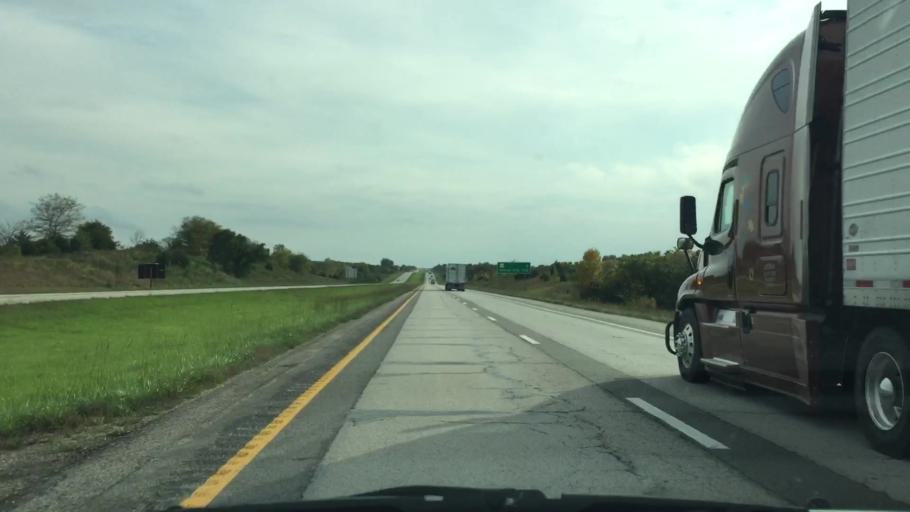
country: US
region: Iowa
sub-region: Decatur County
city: Lamoni
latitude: 40.4532
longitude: -93.9809
